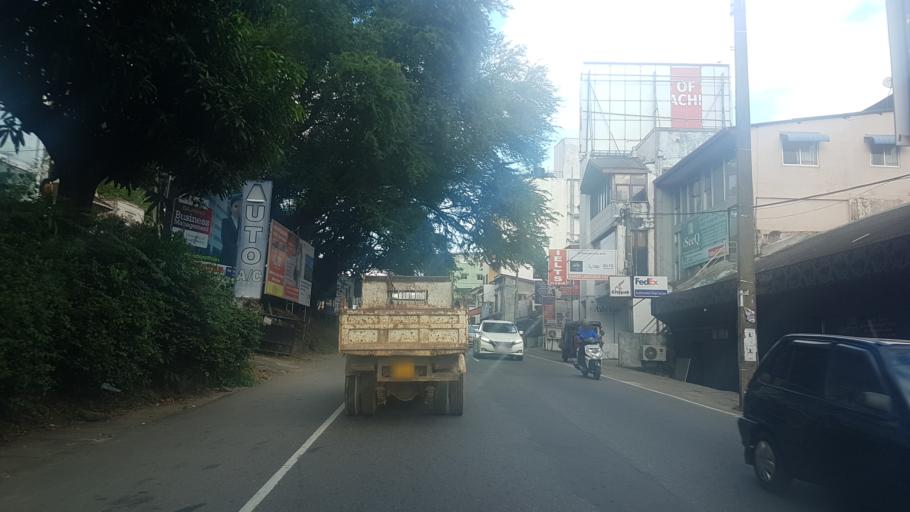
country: LK
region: Central
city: Kandy
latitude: 7.2871
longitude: 80.6276
